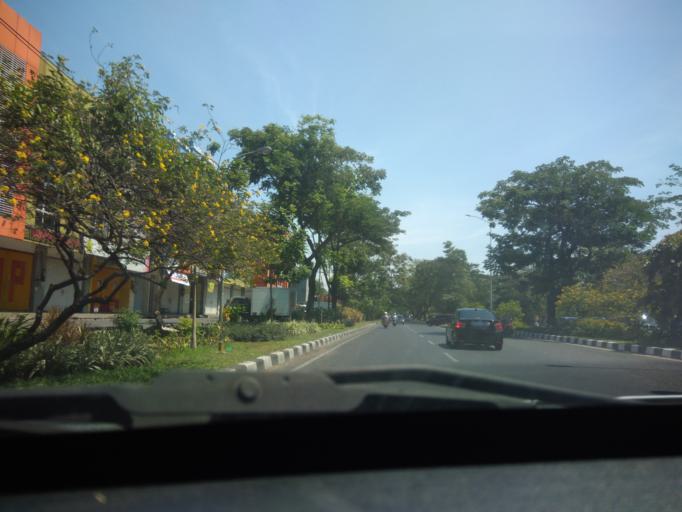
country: ID
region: East Java
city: Semampir
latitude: -7.3041
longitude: 112.7813
